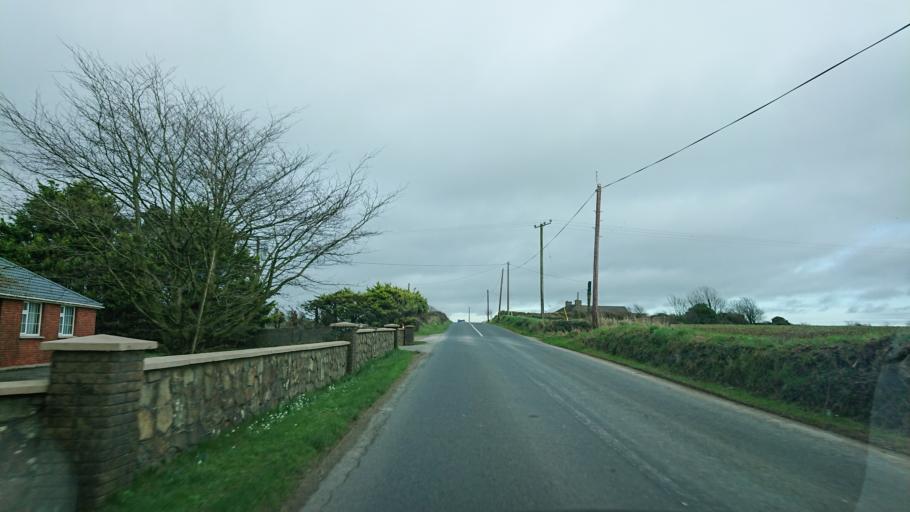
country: IE
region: Munster
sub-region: Waterford
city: Portlaw
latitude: 52.1861
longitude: -7.2940
